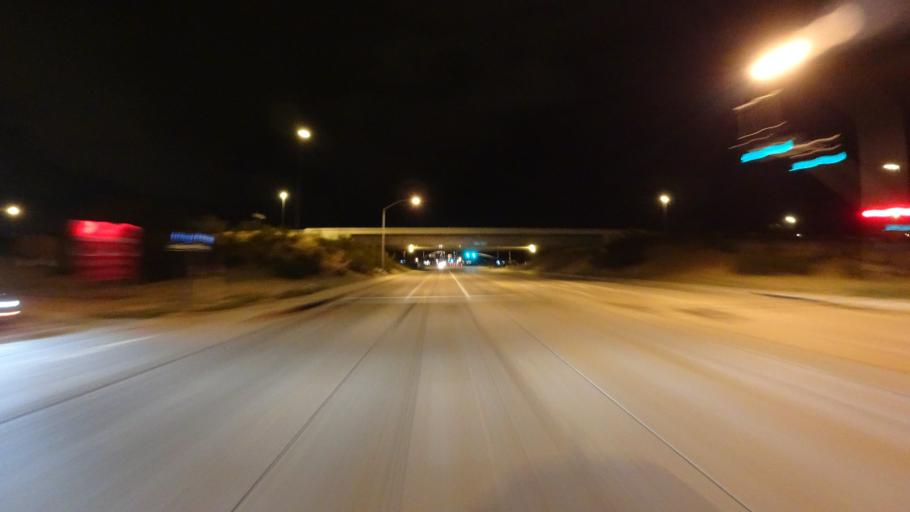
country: US
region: Arizona
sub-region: Pinal County
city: Apache Junction
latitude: 33.3859
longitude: -111.5981
